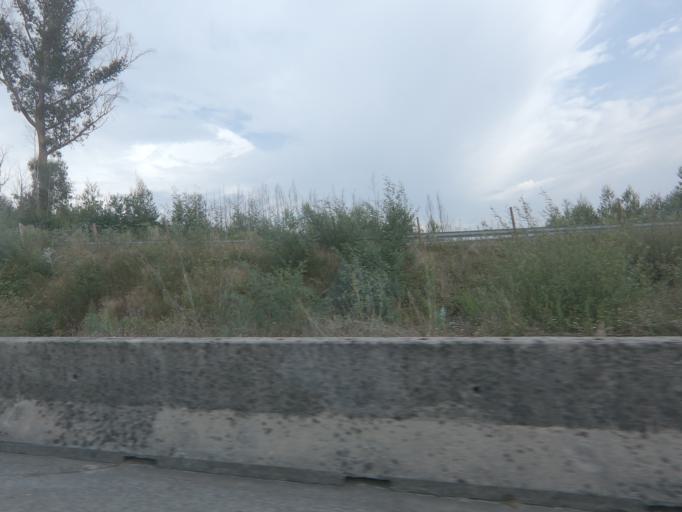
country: PT
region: Viseu
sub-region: Mortagua
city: Mortagua
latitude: 40.3451
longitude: -8.2110
